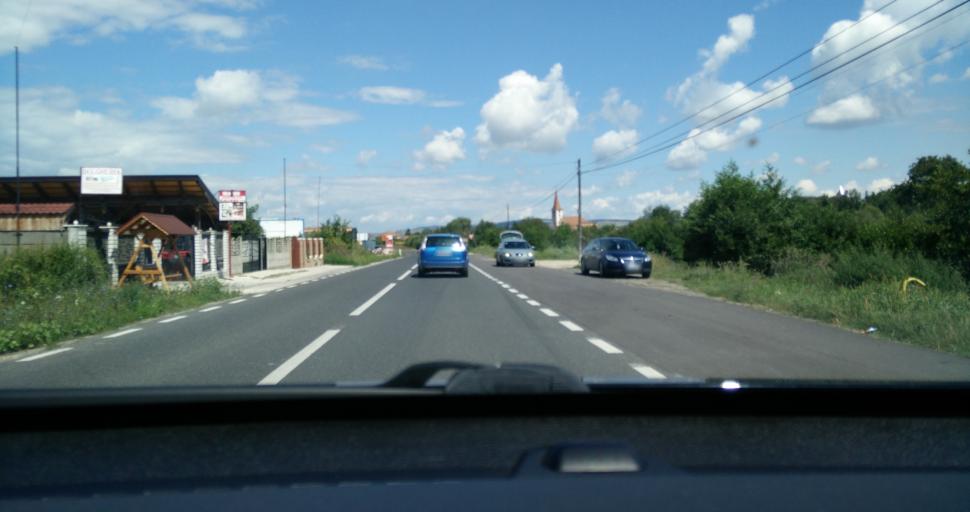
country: RO
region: Alba
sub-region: Municipiul Sebes
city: Petresti
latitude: 45.9156
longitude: 23.5553
